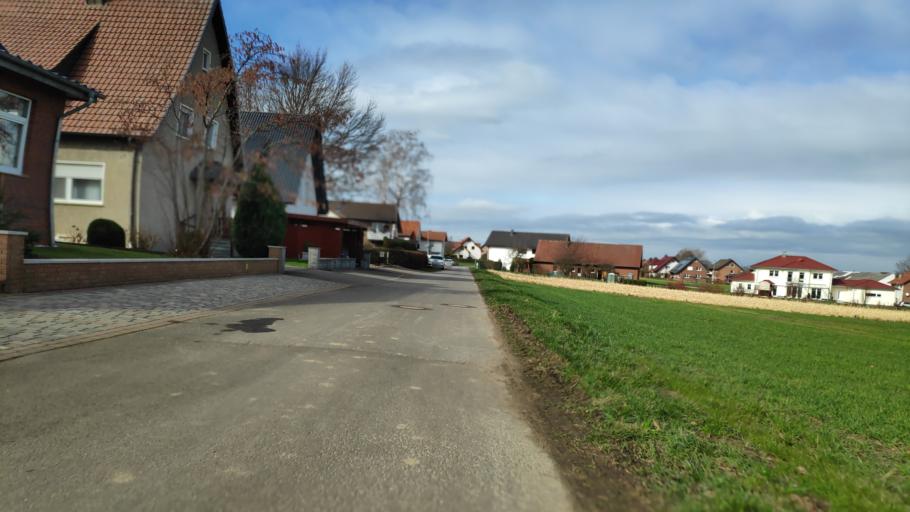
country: DE
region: North Rhine-Westphalia
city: Bad Oeynhausen
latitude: 52.2719
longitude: 8.7977
